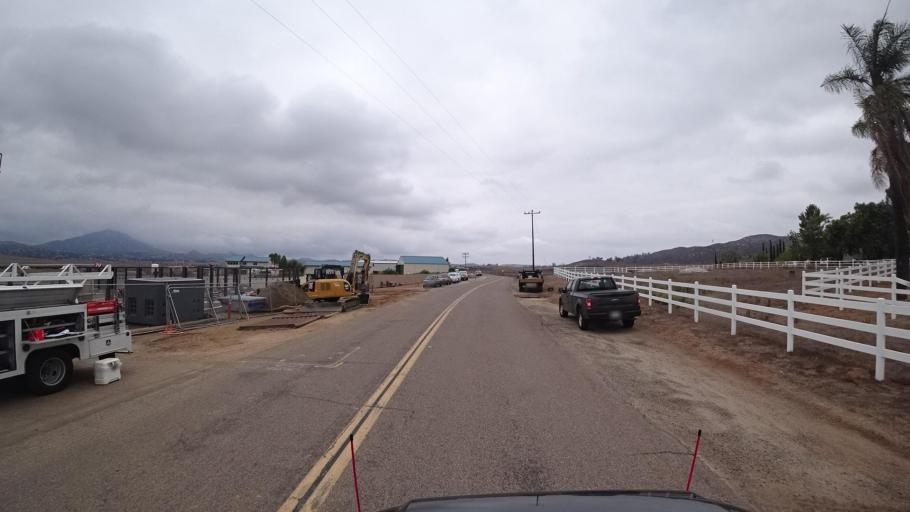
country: US
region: California
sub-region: San Diego County
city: Ramona
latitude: 33.0406
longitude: -116.9099
